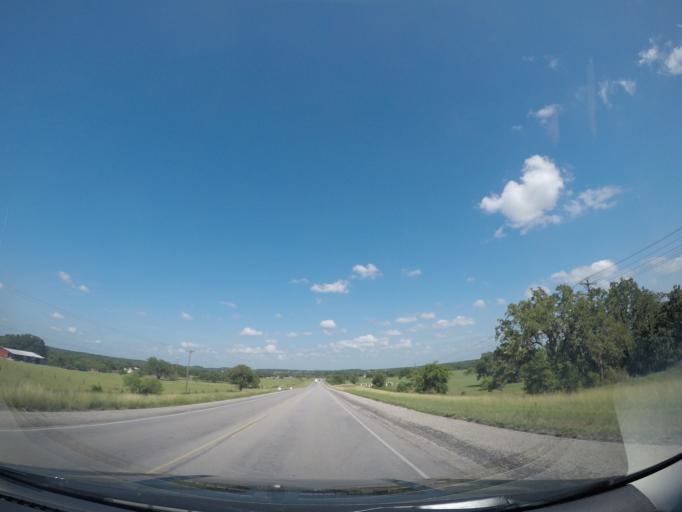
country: US
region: Texas
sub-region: Caldwell County
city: Luling
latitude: 29.5367
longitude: -97.7369
